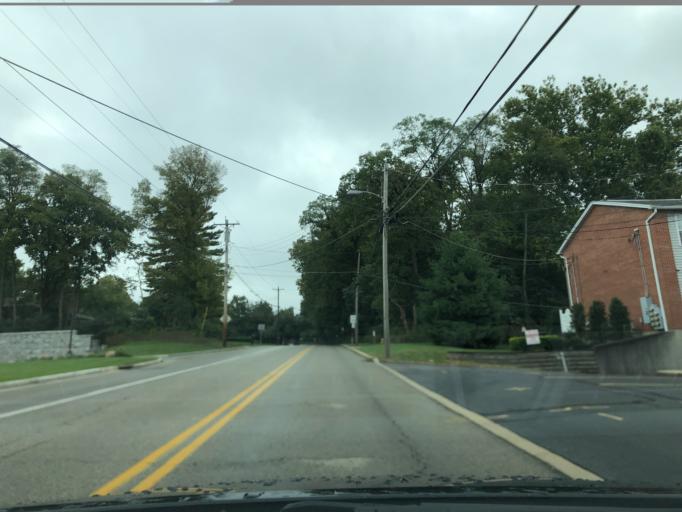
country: US
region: Ohio
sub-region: Hamilton County
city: Sharonville
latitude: 39.2829
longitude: -84.4009
